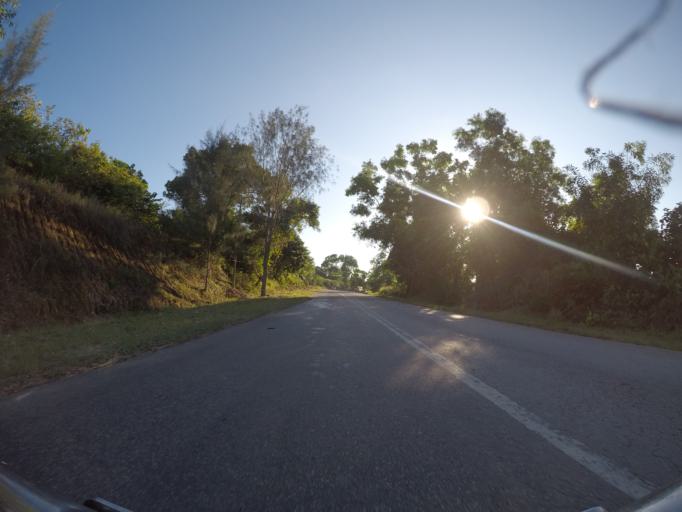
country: TZ
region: Pemba South
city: Uwelini
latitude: -5.3758
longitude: 39.6731
